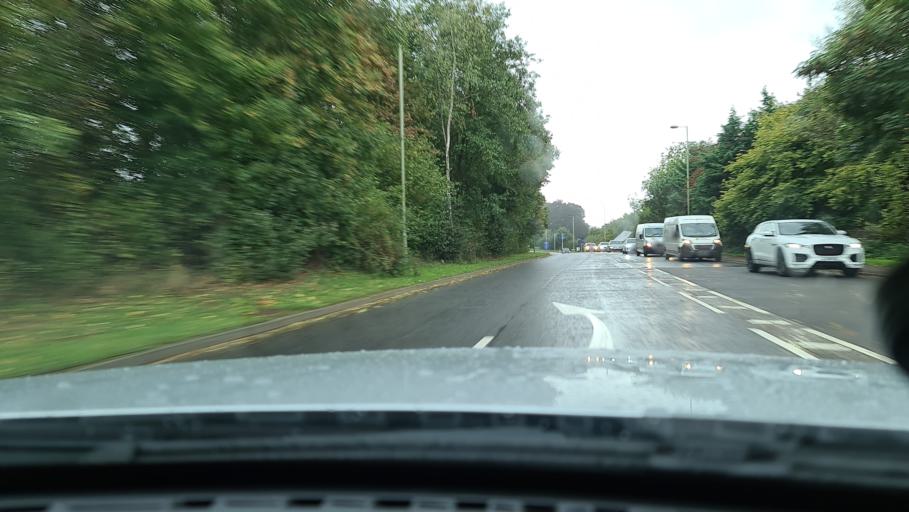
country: GB
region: England
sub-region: Oxfordshire
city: Adderbury
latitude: 52.0363
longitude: -1.3203
